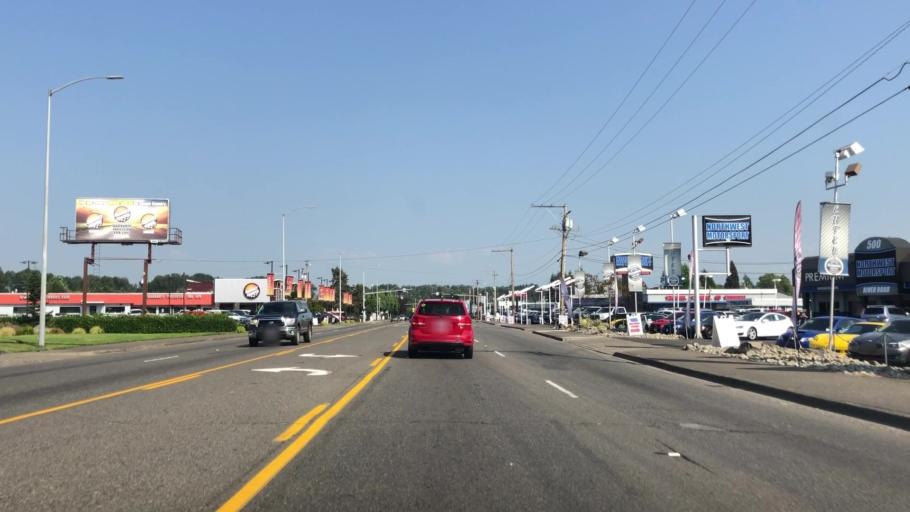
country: US
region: Washington
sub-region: Pierce County
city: Puyallup
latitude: 47.2005
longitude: -122.3009
